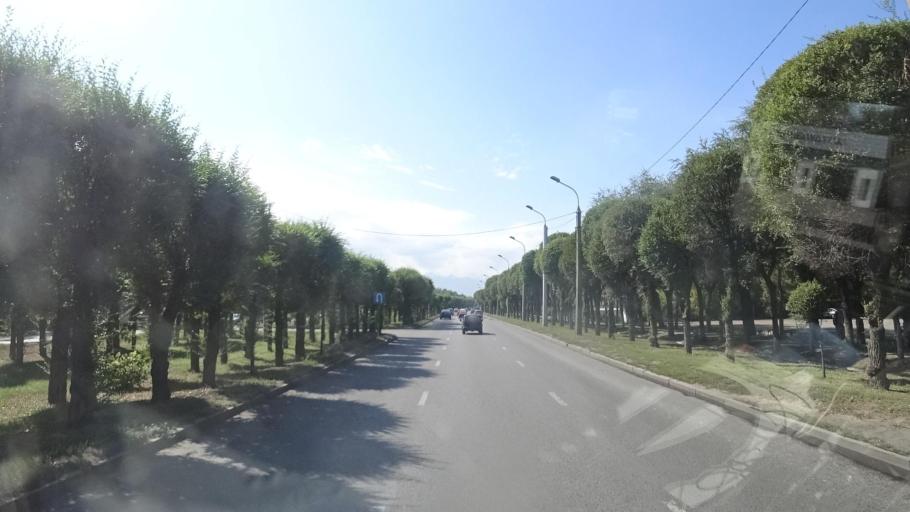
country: KZ
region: Almaty Oblysy
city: Pervomayskiy
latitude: 43.3370
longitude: 76.9819
